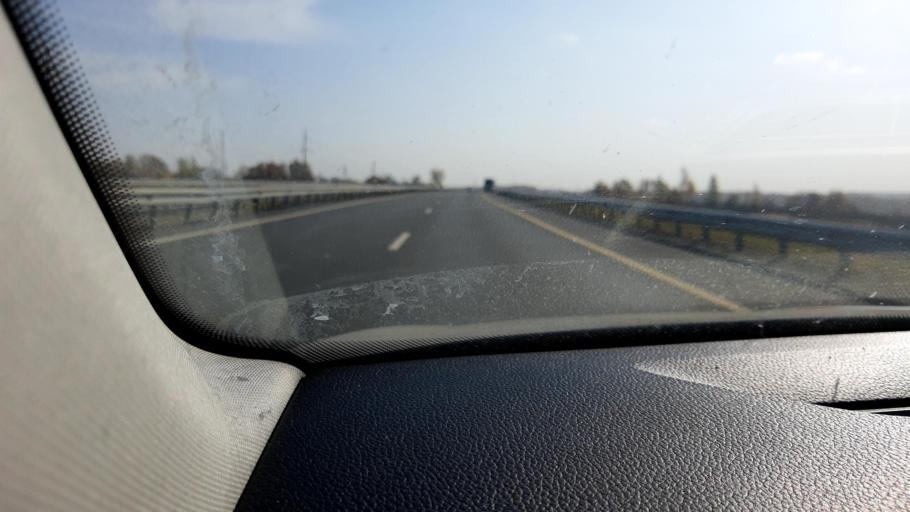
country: RU
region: Moskovskaya
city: Kashira
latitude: 54.7766
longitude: 38.1319
